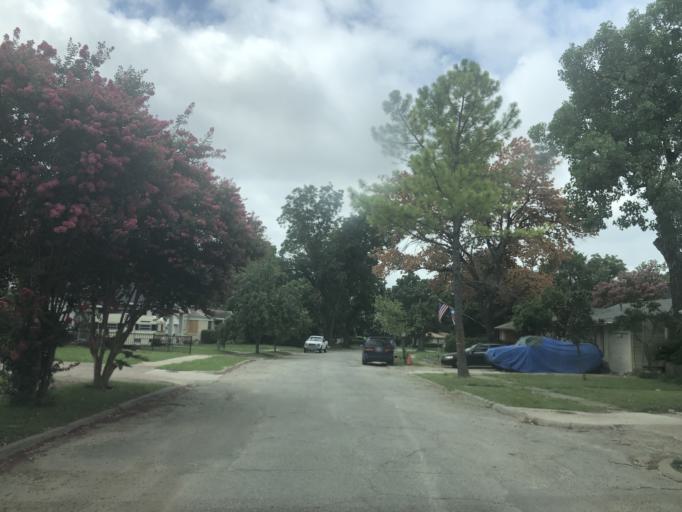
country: US
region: Texas
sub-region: Dallas County
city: University Park
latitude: 32.8647
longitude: -96.8489
